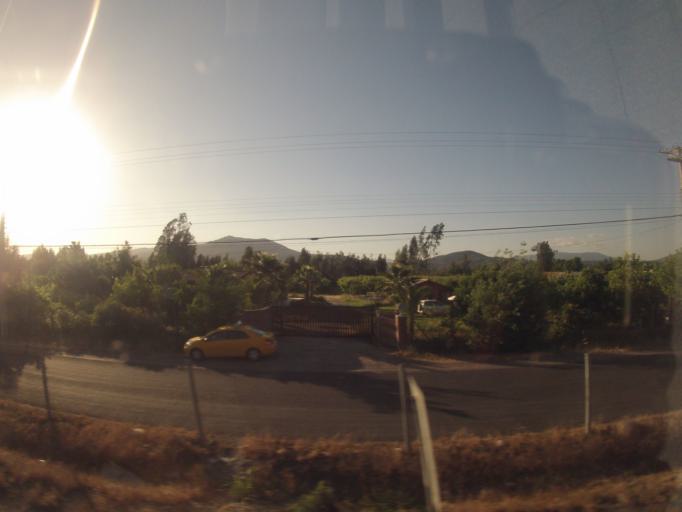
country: CL
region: O'Higgins
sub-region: Provincia de Colchagua
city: Chimbarongo
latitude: -34.6879
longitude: -71.0130
